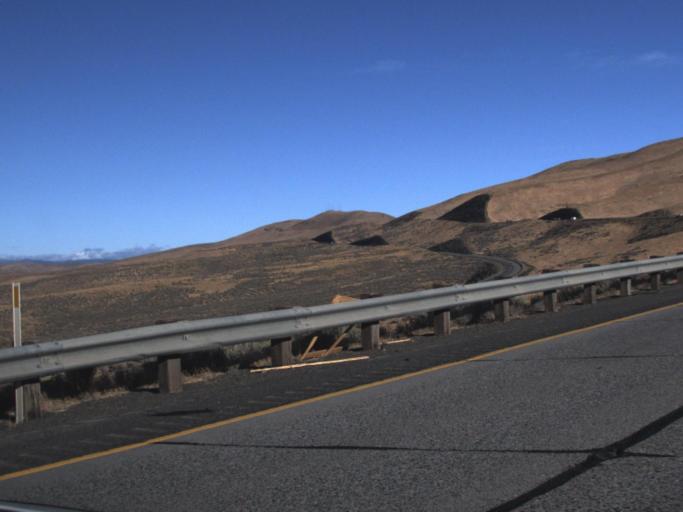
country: US
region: Washington
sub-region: Kittitas County
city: Kittitas
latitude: 46.8552
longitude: -120.3925
